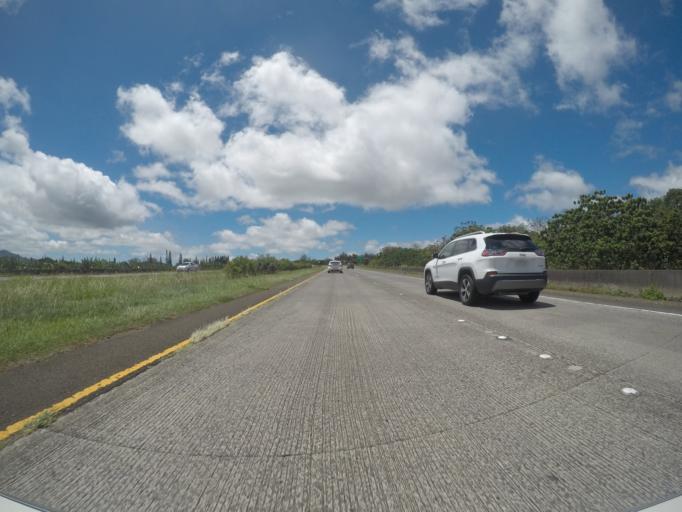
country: US
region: Hawaii
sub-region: Honolulu County
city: Wahiawa
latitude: 21.4850
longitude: -158.0253
